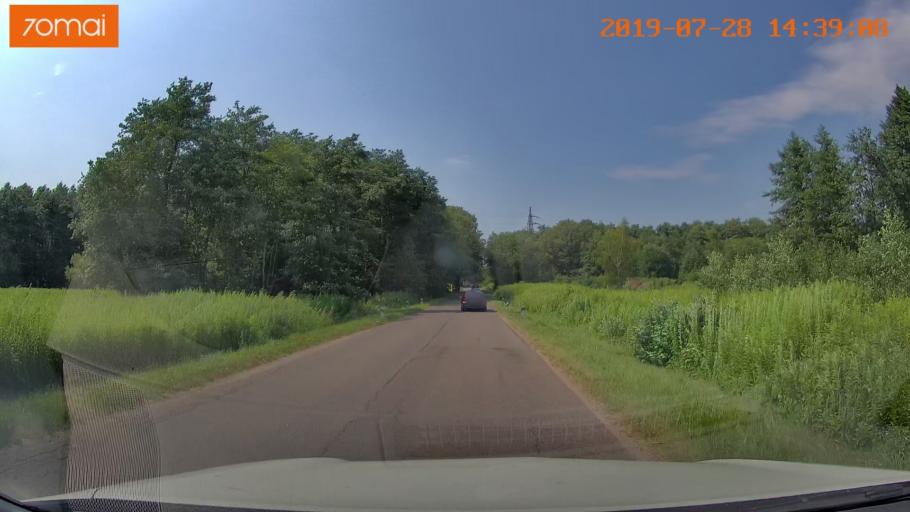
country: RU
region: Kaliningrad
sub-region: Gorod Kaliningrad
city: Yantarnyy
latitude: 54.8468
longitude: 19.9738
